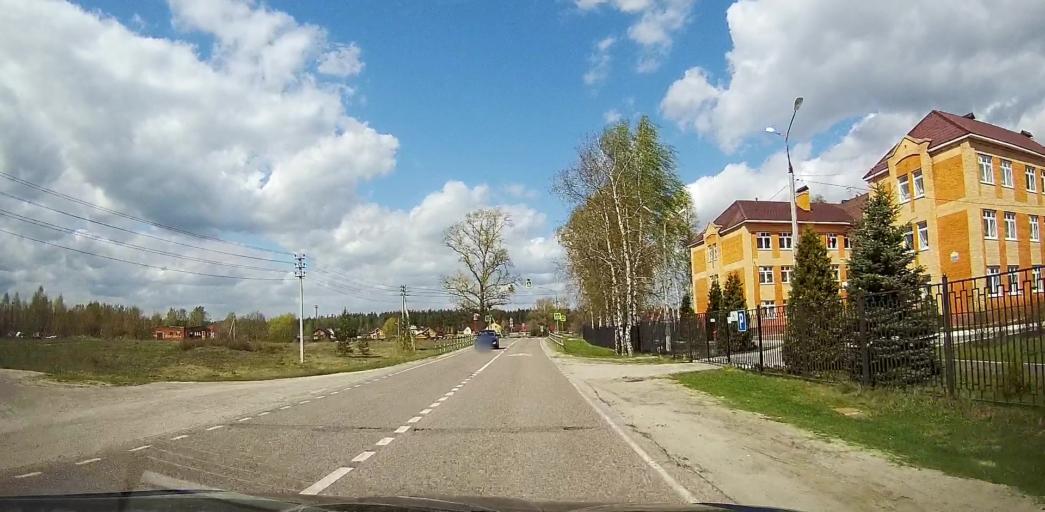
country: RU
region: Moskovskaya
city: Davydovo
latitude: 55.5580
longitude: 38.8137
